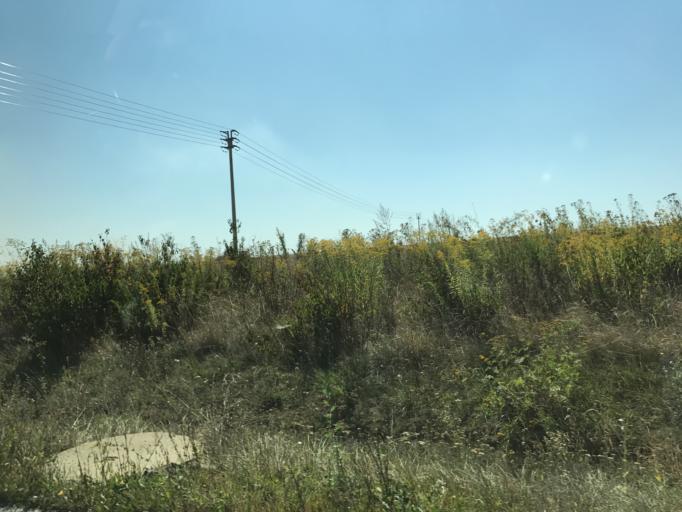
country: SK
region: Kosicky
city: Kosice
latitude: 48.6870
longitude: 21.2258
